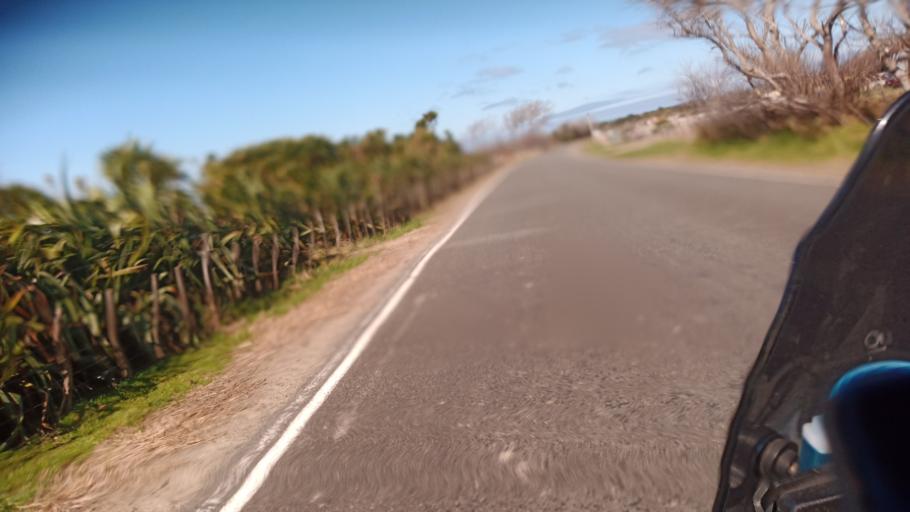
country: NZ
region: Gisborne
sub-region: Gisborne District
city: Gisborne
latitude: -39.0532
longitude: 177.8839
